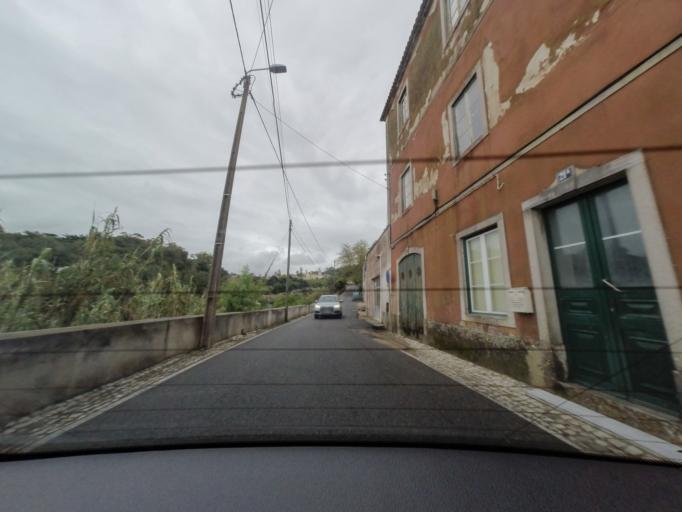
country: PT
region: Lisbon
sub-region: Sintra
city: Sintra
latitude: 38.8008
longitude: -9.3932
